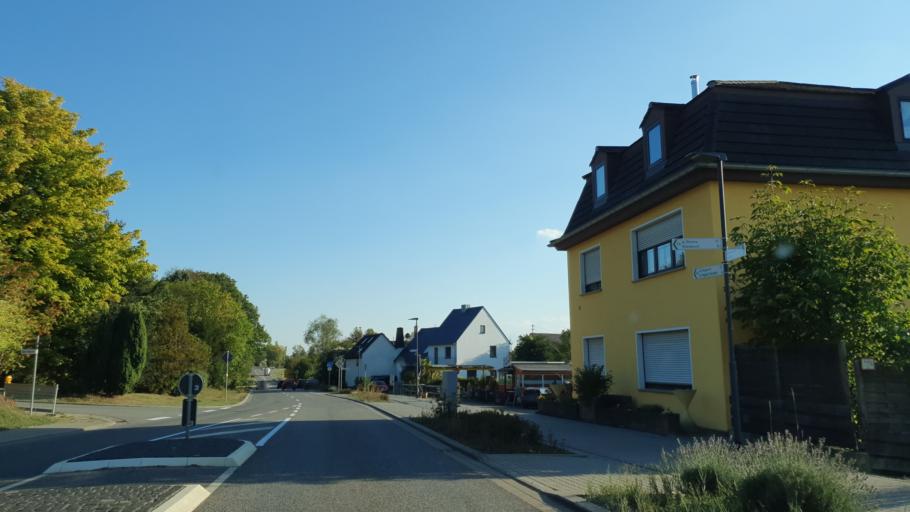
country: DE
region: Rheinland-Pfalz
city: Nortershausen
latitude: 50.2378
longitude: 7.5119
